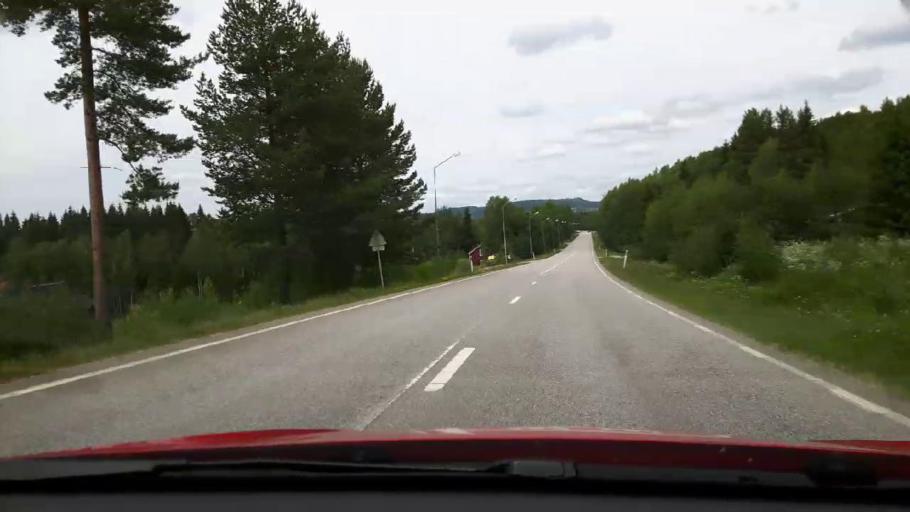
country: SE
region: Jaemtland
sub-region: Harjedalens Kommun
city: Sveg
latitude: 62.0669
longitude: 14.2730
